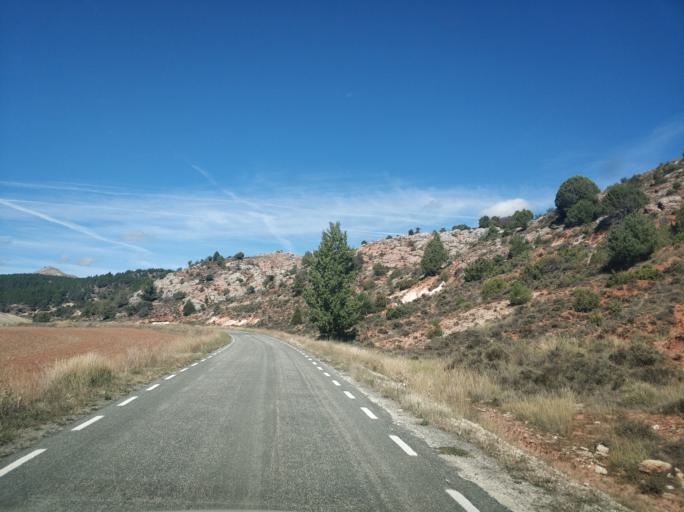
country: ES
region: Castille and Leon
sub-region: Provincia de Soria
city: Espeja de San Marcelino
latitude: 41.8113
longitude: -3.2242
